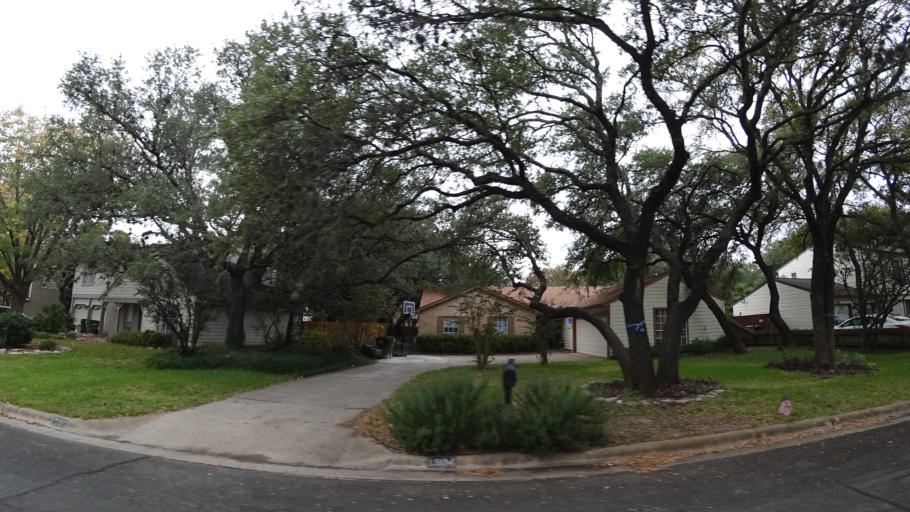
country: US
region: Texas
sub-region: Williamson County
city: Round Rock
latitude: 30.4921
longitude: -97.6982
